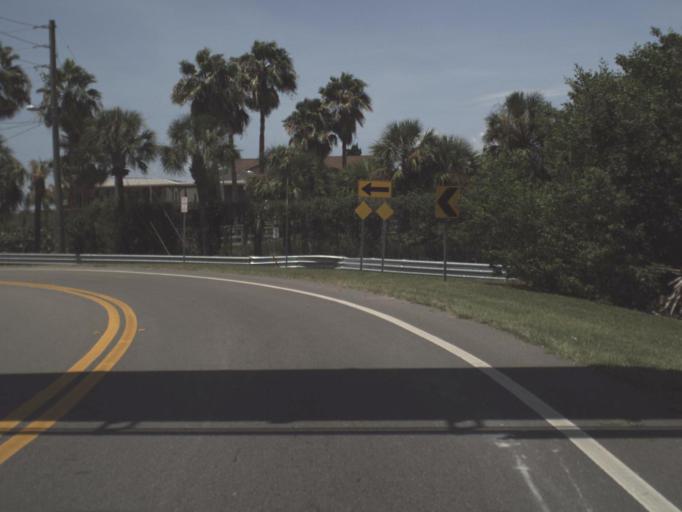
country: US
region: Florida
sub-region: Hillsborough County
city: Apollo Beach
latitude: 27.7927
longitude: -82.4004
